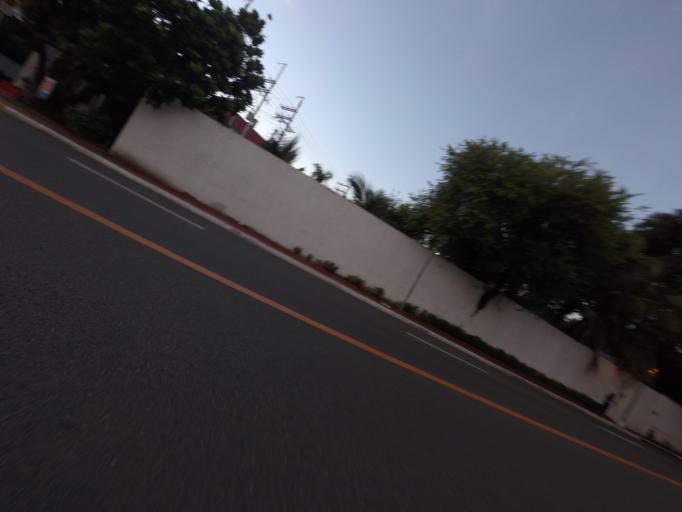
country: PH
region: Metro Manila
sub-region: City of Manila
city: Quiapo
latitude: 14.5937
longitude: 120.9932
